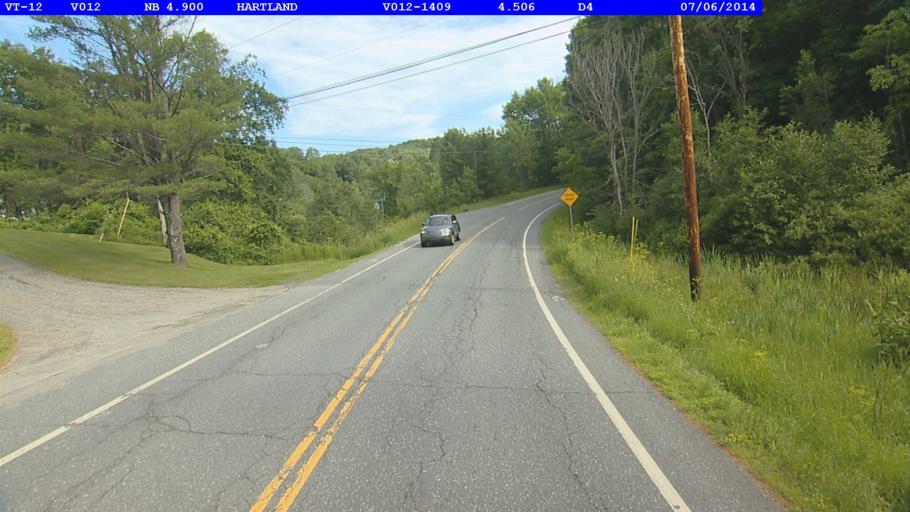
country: US
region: Vermont
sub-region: Windsor County
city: Woodstock
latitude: 43.5827
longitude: -72.4489
